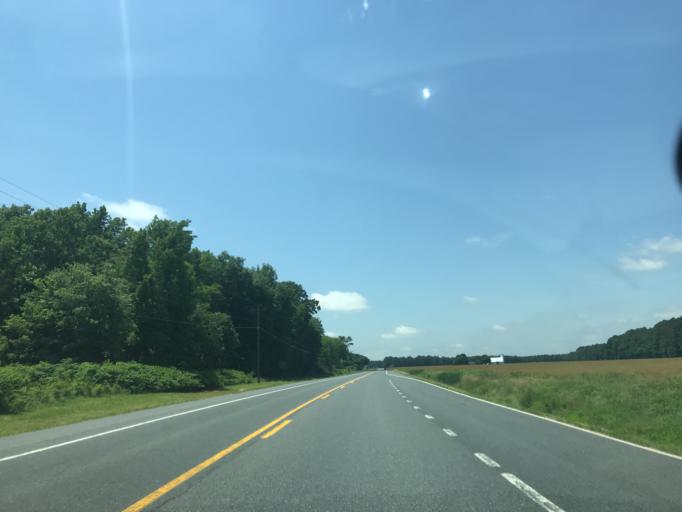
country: US
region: Maryland
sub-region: Caroline County
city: Federalsburg
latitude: 38.6313
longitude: -75.7629
